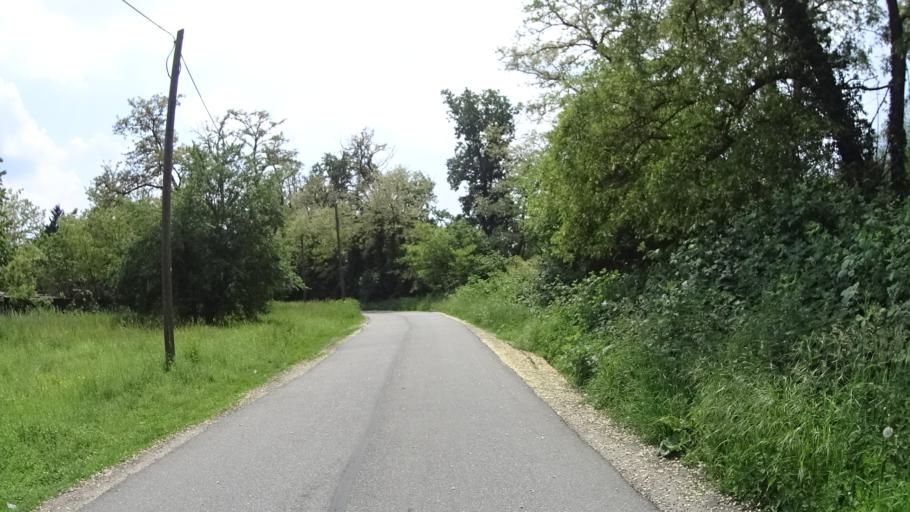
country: DE
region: Baden-Wuerttemberg
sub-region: Karlsruhe Region
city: Rheinstetten
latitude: 48.9911
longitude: 8.3311
